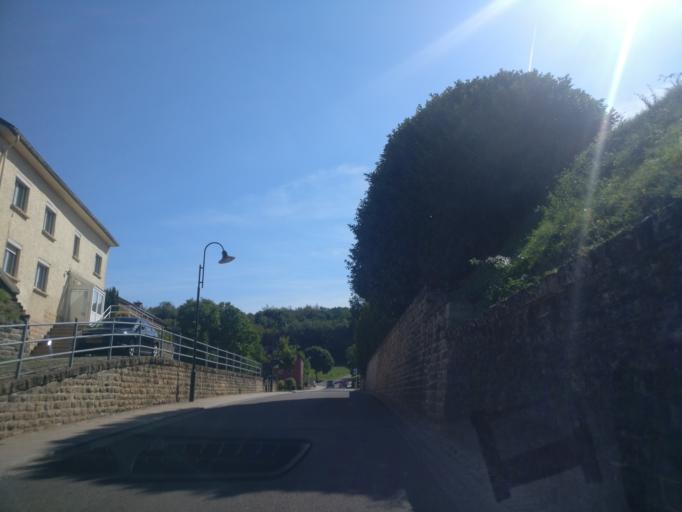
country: LU
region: Grevenmacher
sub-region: Canton de Grevenmacher
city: Flaxweiler
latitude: 49.6630
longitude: 6.3459
